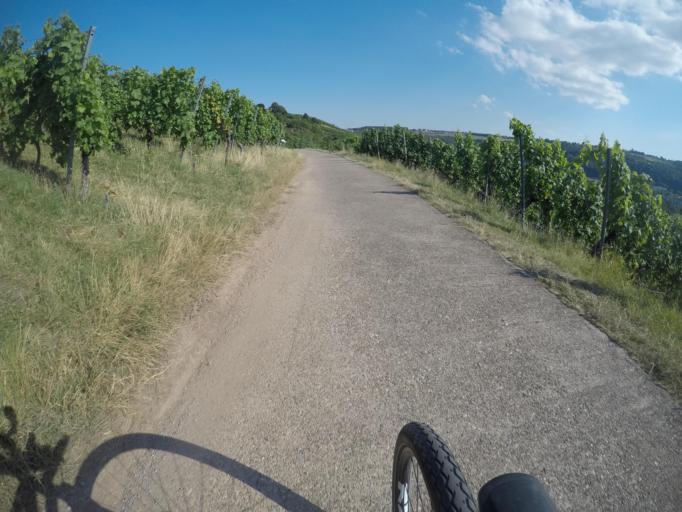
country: DE
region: Baden-Wuerttemberg
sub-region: Regierungsbezirk Stuttgart
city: Esslingen
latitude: 48.7468
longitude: 9.2810
